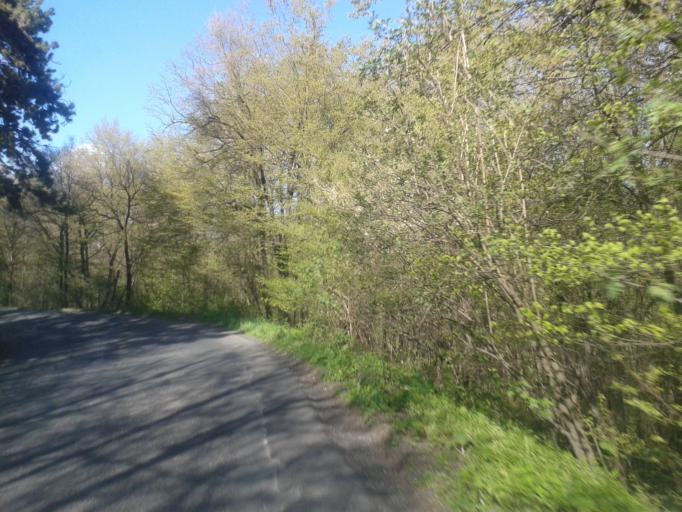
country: CZ
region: Central Bohemia
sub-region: Okres Beroun
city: Beroun
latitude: 49.9081
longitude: 14.0748
